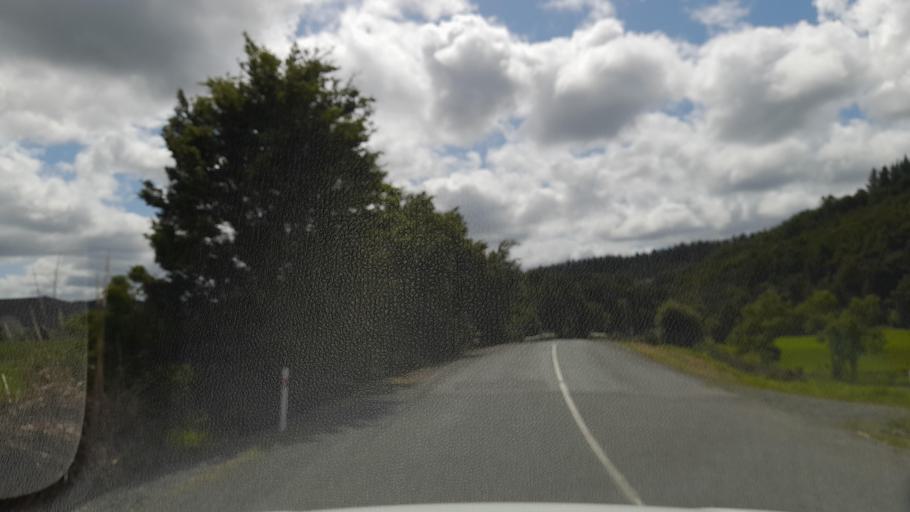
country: NZ
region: Northland
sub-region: Whangarei
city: Maungatapere
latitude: -35.6963
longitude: 174.0442
